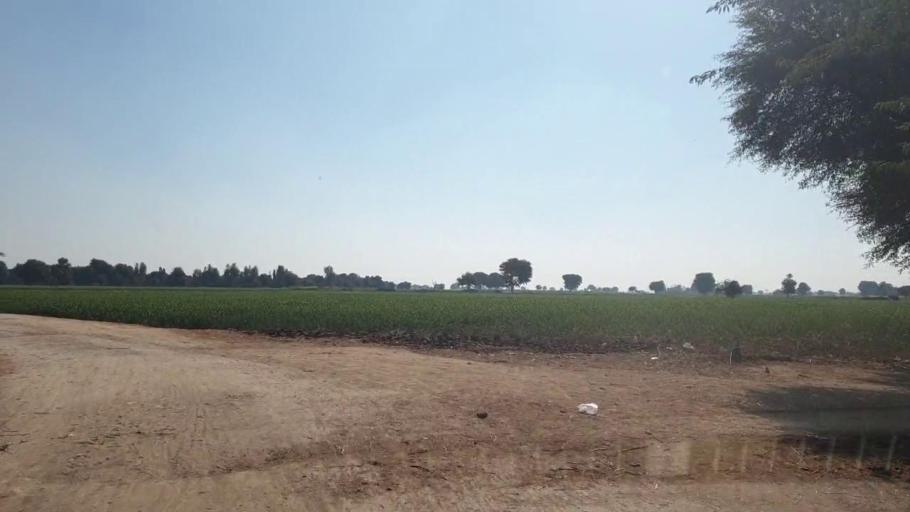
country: PK
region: Sindh
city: Shahpur Chakar
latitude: 26.1253
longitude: 68.6400
